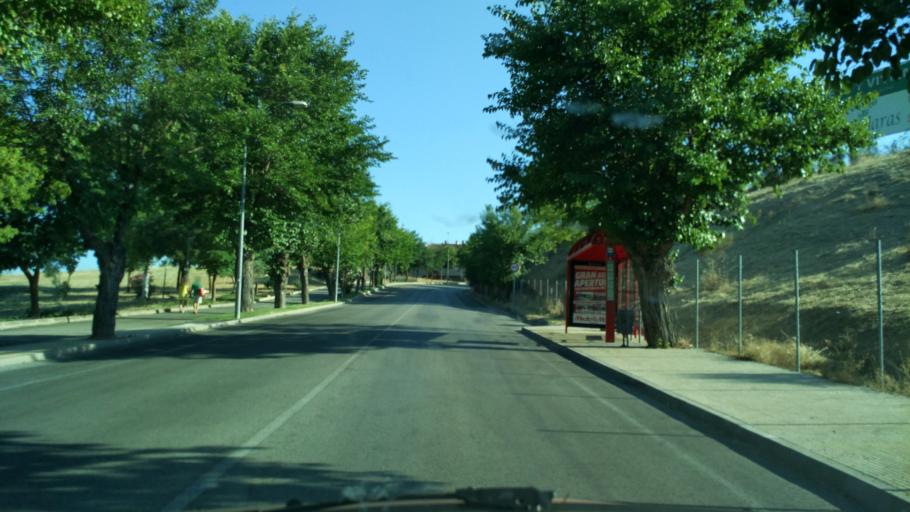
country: ES
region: Madrid
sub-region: Provincia de Madrid
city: San Agustin de Guadalix
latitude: 40.6855
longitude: -3.6110
